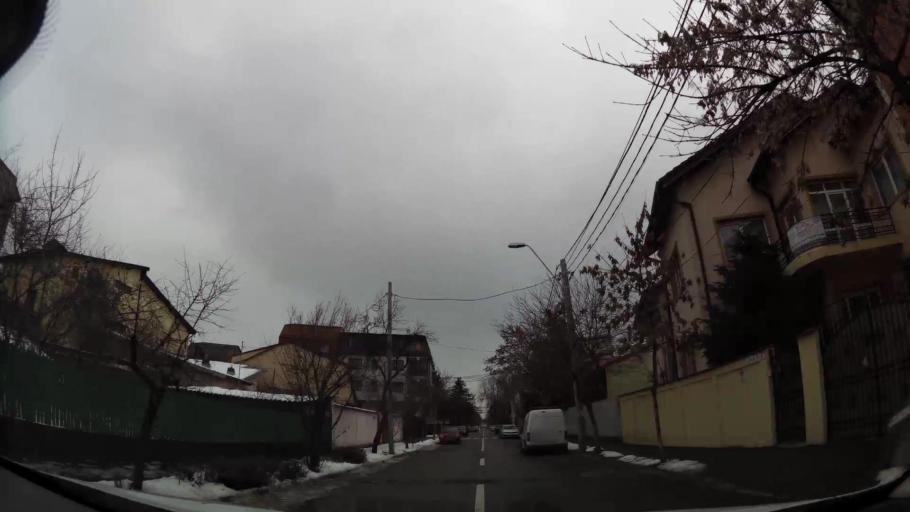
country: RO
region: Ilfov
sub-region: Comuna Chiajna
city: Rosu
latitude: 44.4872
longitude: 26.0305
